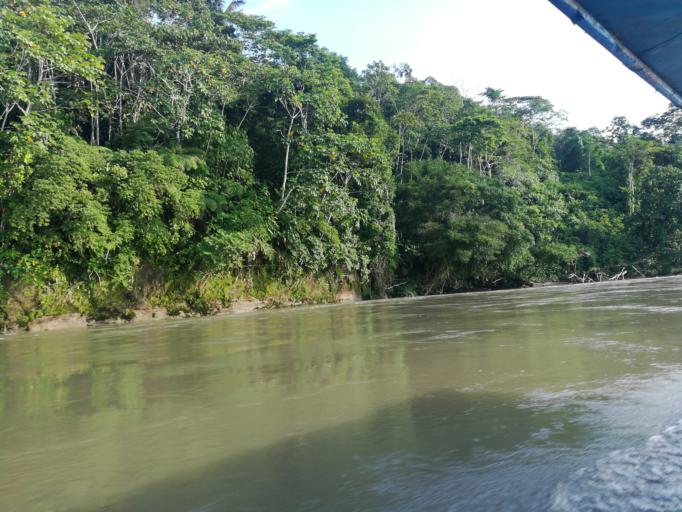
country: EC
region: Orellana
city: Boca Suno
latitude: -0.8645
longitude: -77.2488
